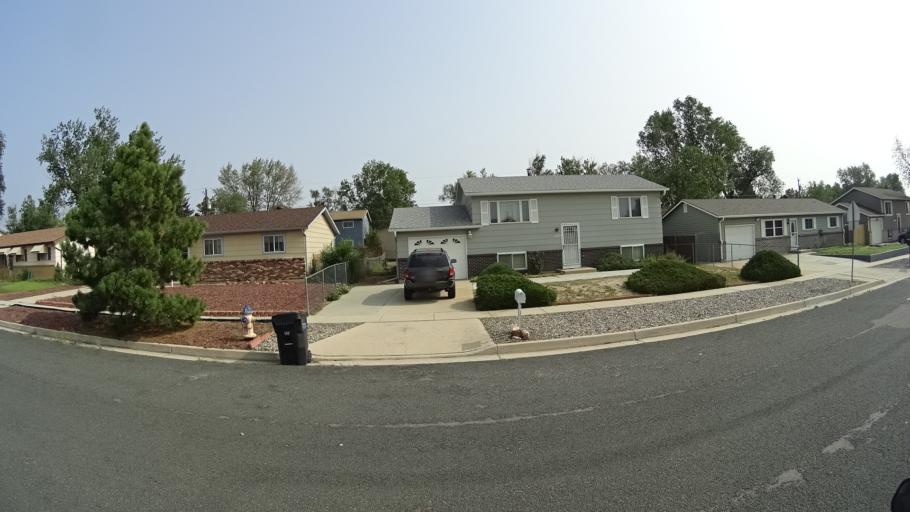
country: US
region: Colorado
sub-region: El Paso County
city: Stratmoor
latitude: 38.7958
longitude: -104.7650
